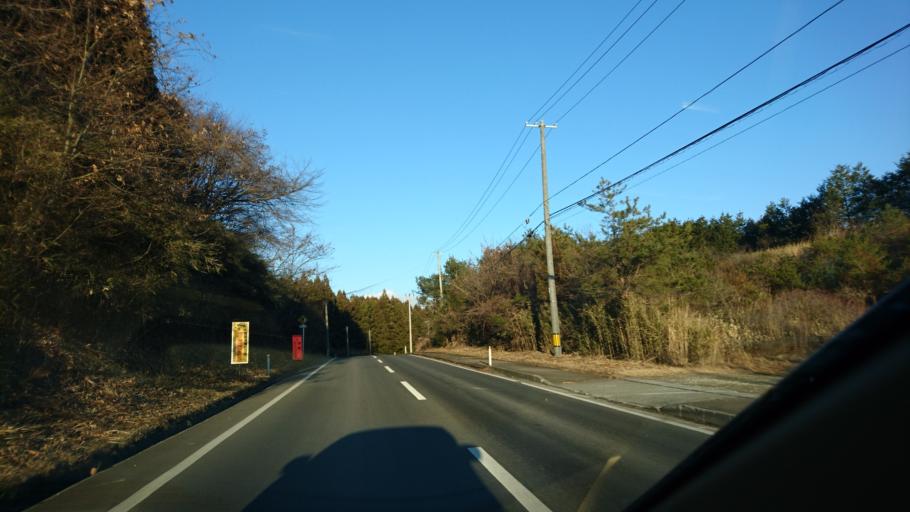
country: JP
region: Miyagi
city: Furukawa
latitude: 38.6591
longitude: 140.8989
